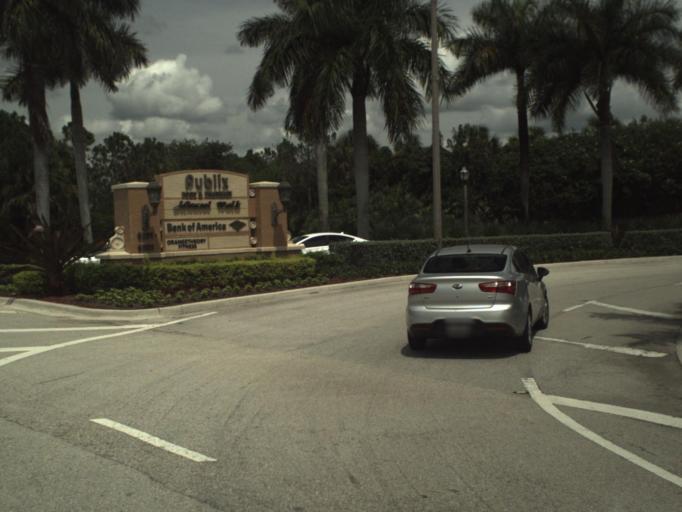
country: US
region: Florida
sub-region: Palm Beach County
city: Palm Beach Gardens
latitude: 26.8392
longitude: -80.1338
